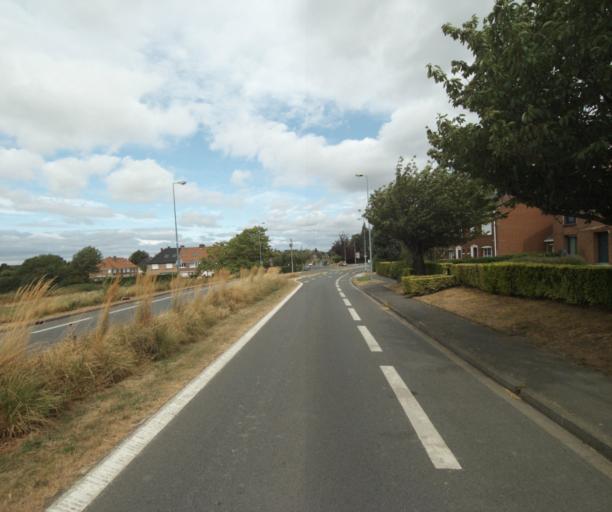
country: FR
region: Nord-Pas-de-Calais
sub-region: Departement du Nord
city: Linselles
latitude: 50.7327
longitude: 3.0890
